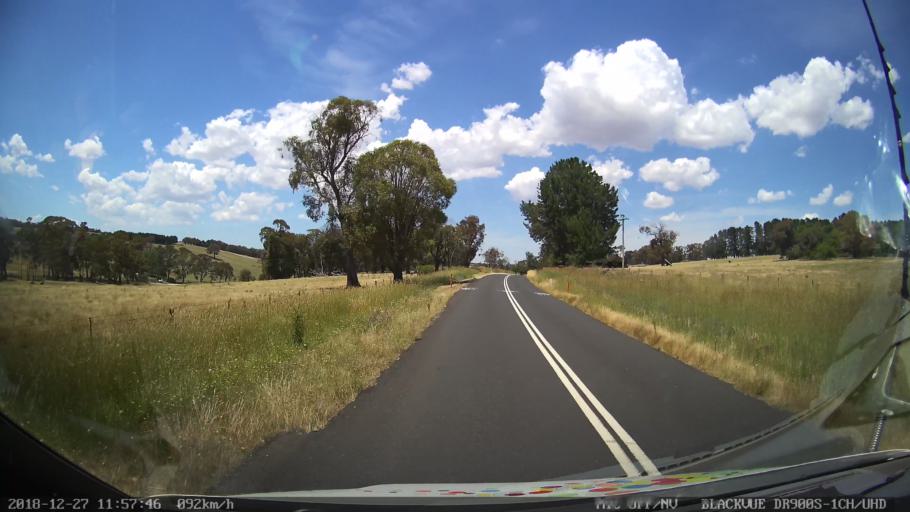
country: AU
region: New South Wales
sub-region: Blayney
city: Blayney
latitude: -33.7159
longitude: 149.3884
